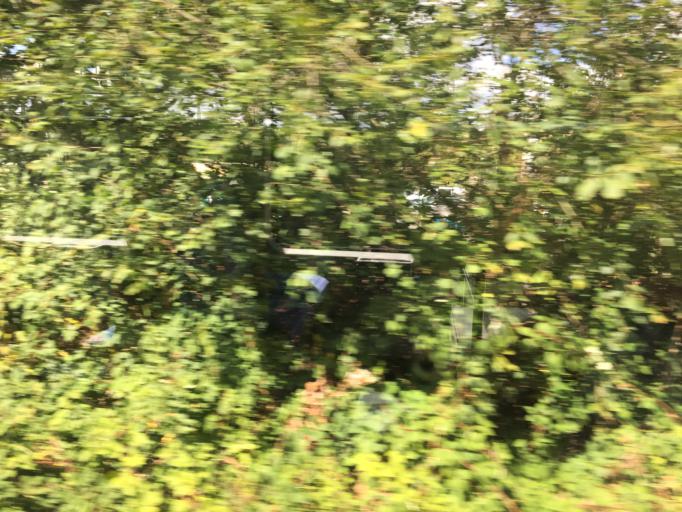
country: DE
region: North Rhine-Westphalia
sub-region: Regierungsbezirk Arnsberg
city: Dortmund
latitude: 51.5105
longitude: 7.4019
